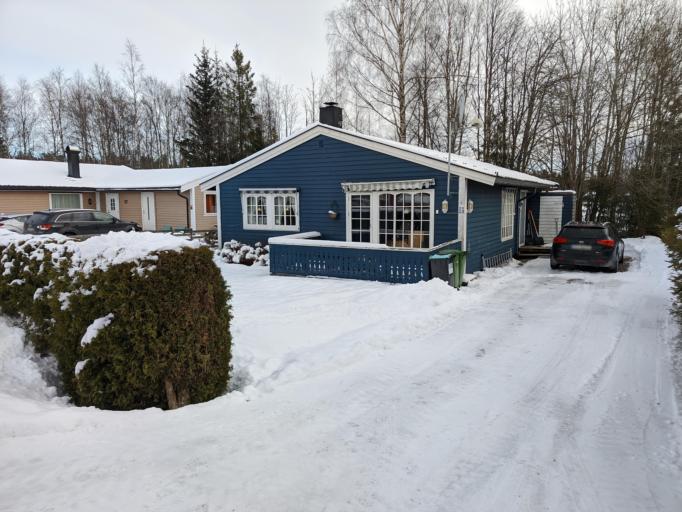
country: NO
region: Akershus
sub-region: Nannestad
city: Teigebyen
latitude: 60.2241
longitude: 11.0234
